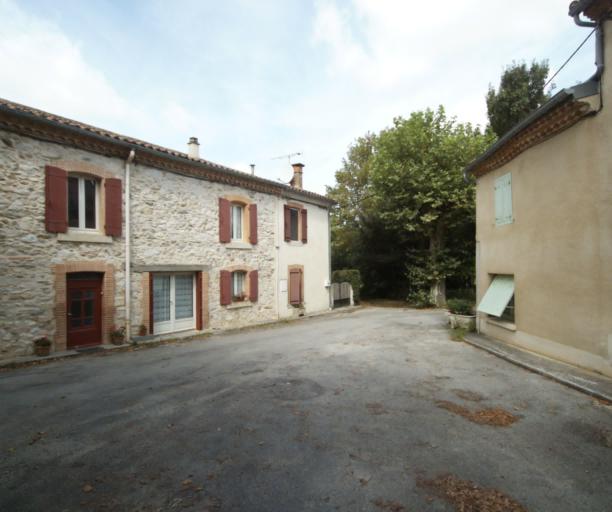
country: FR
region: Midi-Pyrenees
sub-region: Departement du Tarn
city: Soreze
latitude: 43.4661
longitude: 2.1015
